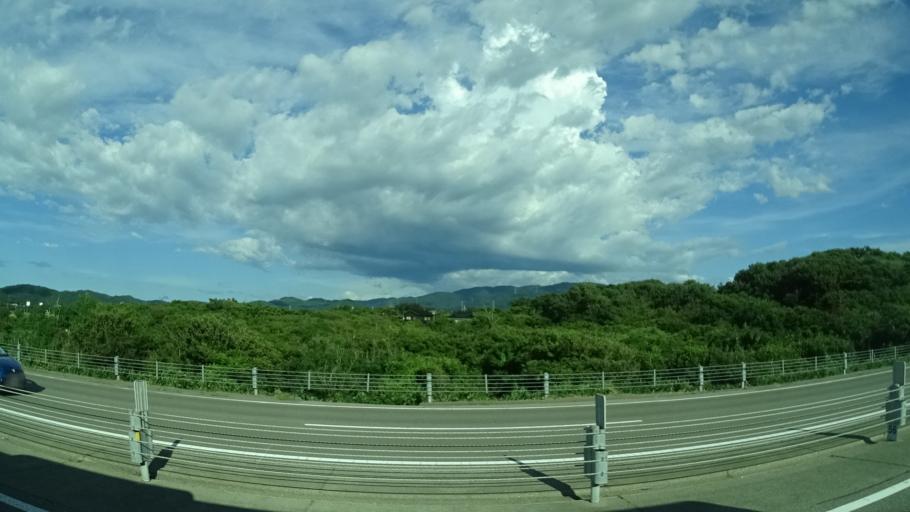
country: JP
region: Ishikawa
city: Hakui
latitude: 36.8225
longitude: 136.7430
